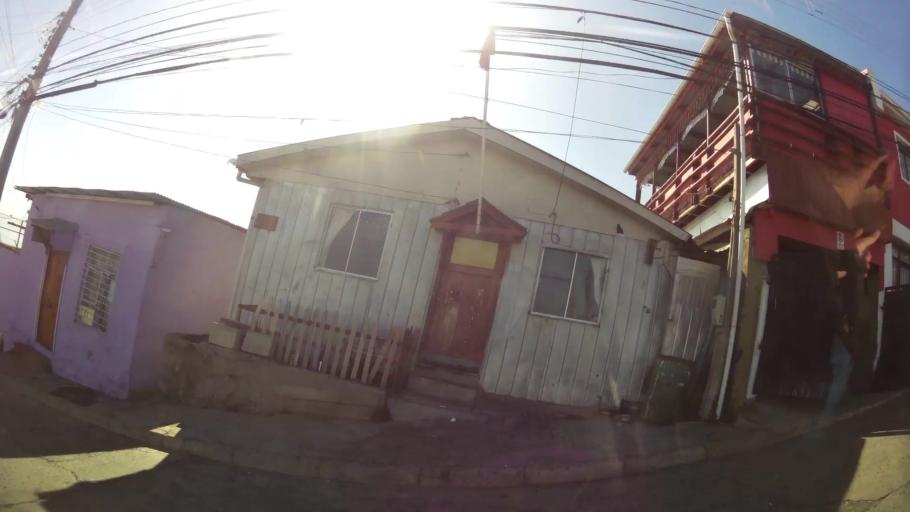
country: CL
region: Valparaiso
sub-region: Provincia de Valparaiso
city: Valparaiso
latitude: -33.0512
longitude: -71.6365
